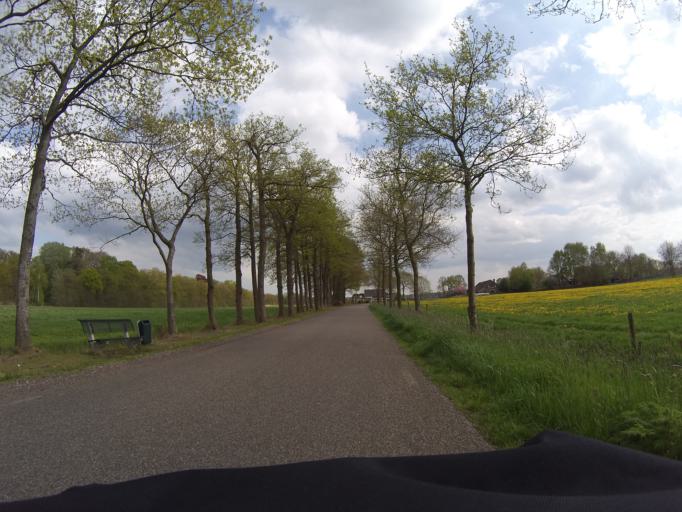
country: NL
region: Gelderland
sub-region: Gemeente Oldebroek
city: Oldebroek
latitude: 52.4610
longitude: 5.9522
